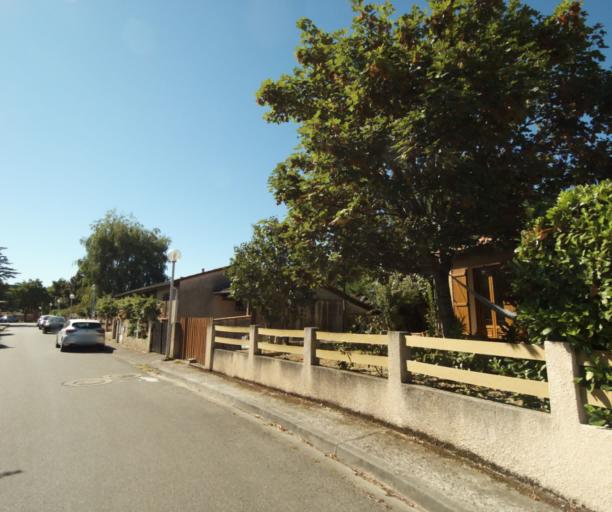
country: FR
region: Midi-Pyrenees
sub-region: Departement de la Haute-Garonne
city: Castanet-Tolosan
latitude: 43.5201
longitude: 1.5036
